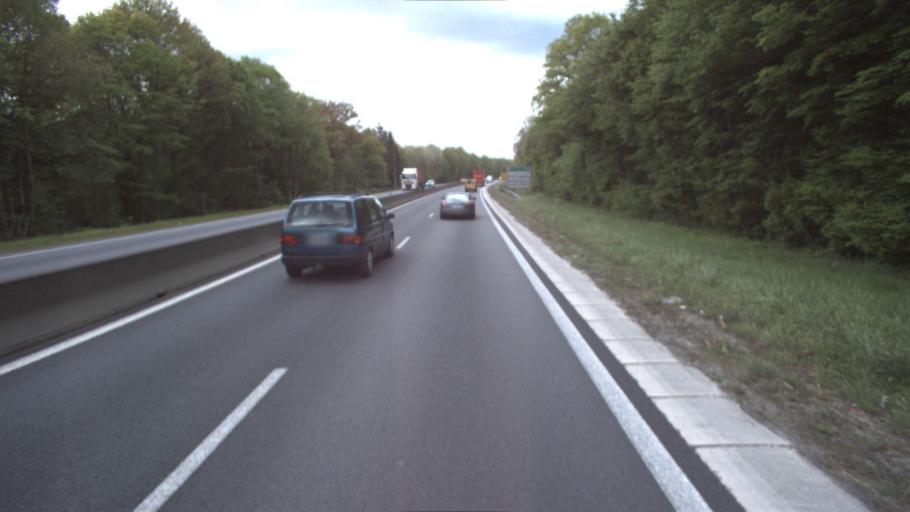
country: FR
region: Ile-de-France
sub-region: Departement de Seine-et-Marne
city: Gretz-Armainvilliers
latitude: 48.7335
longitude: 2.7141
